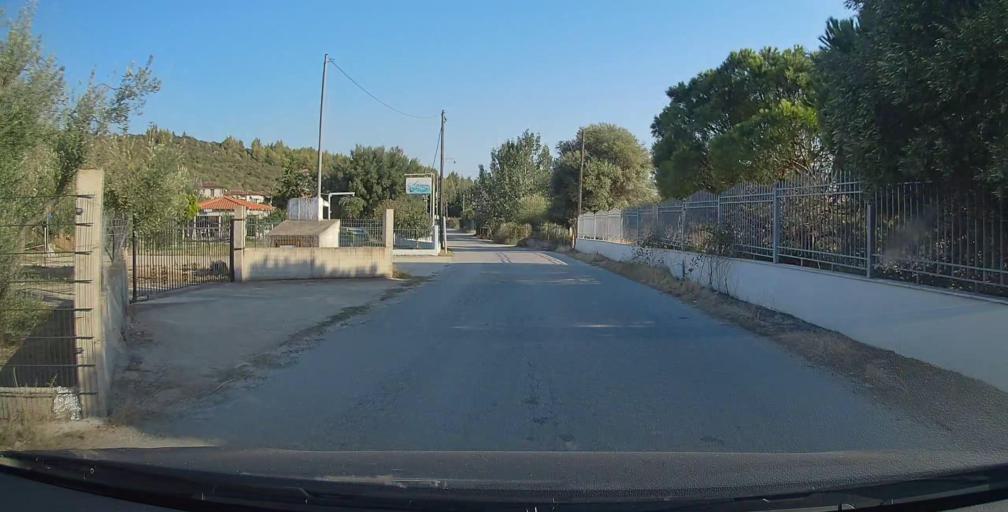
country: GR
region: Central Macedonia
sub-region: Nomos Chalkidikis
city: Sykia
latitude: 39.9968
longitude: 23.8897
